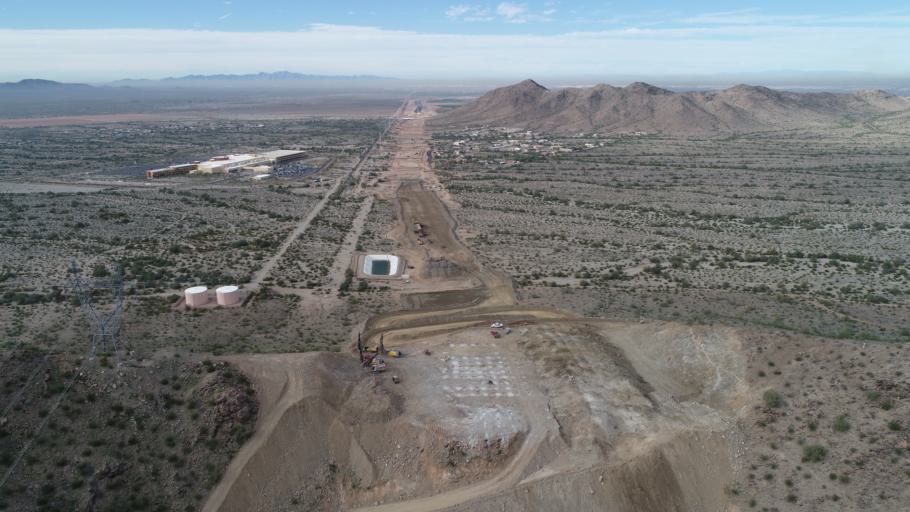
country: US
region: Arizona
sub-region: Maricopa County
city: Laveen
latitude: 33.3035
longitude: -112.1449
